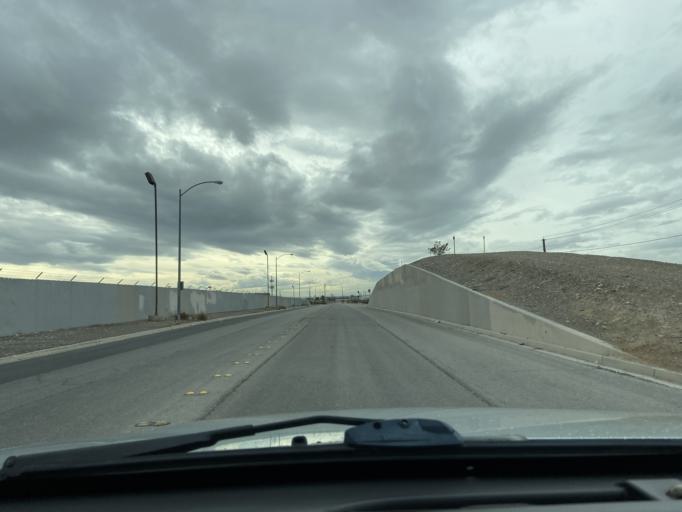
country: US
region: Nevada
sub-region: Clark County
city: Nellis Air Force Base
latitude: 36.2522
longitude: -115.0941
